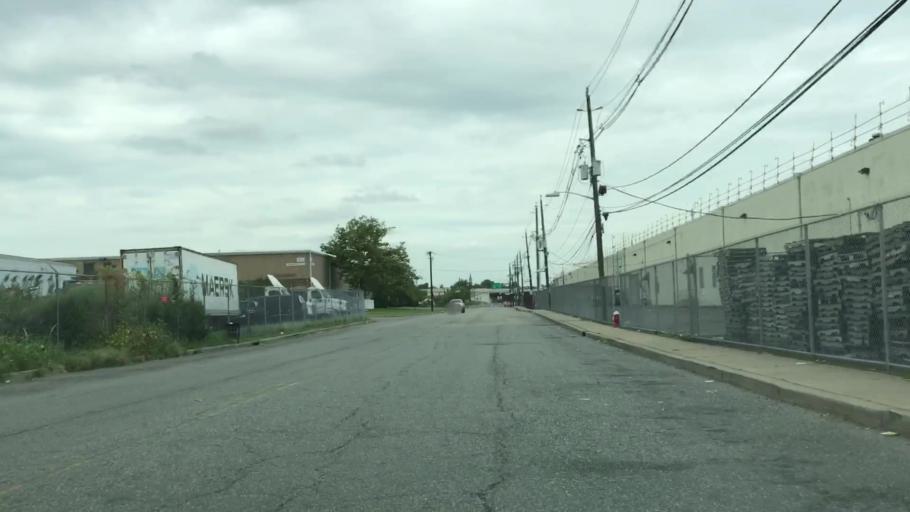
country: US
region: New Jersey
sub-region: Hudson County
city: Bayonne
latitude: 40.6765
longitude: -74.0912
